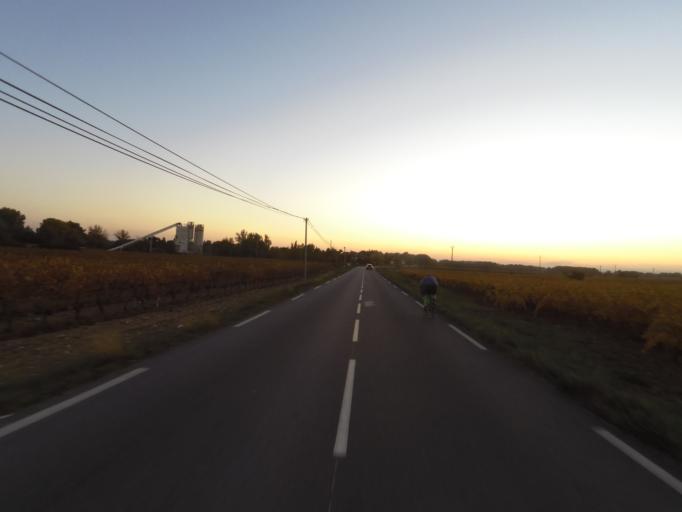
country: FR
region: Provence-Alpes-Cote d'Azur
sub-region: Departement du Vaucluse
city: Caromb
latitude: 44.0820
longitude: 5.1084
